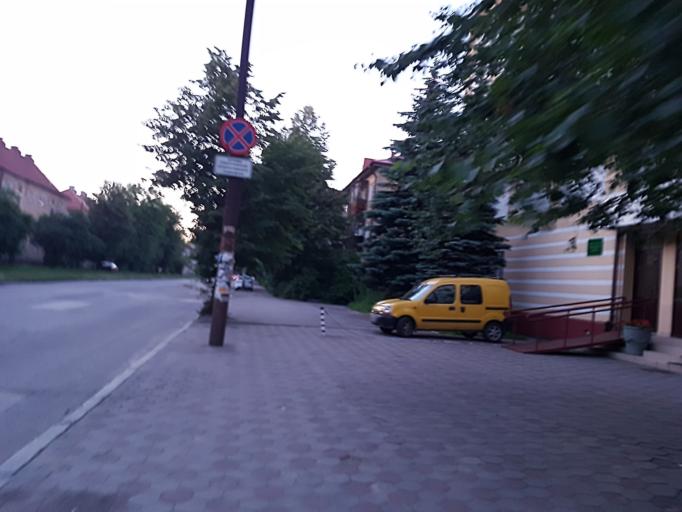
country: RU
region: Kaliningrad
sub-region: Gorod Kaliningrad
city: Kaliningrad
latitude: 54.6892
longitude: 20.5235
